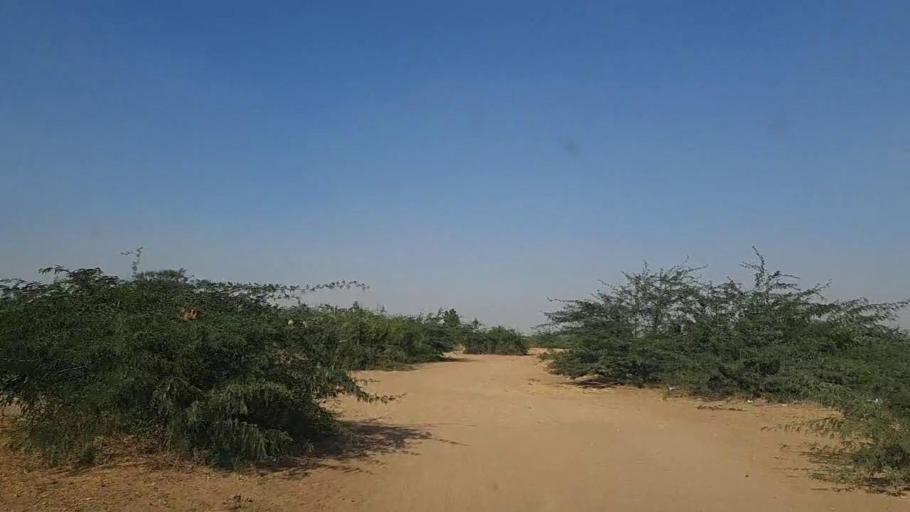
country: PK
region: Sindh
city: Daro Mehar
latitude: 24.9940
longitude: 68.1368
